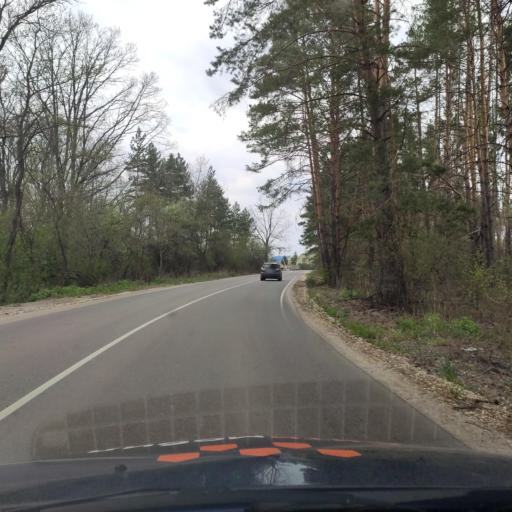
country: RU
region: Voronezj
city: Podgornoye
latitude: 51.8294
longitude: 39.1434
